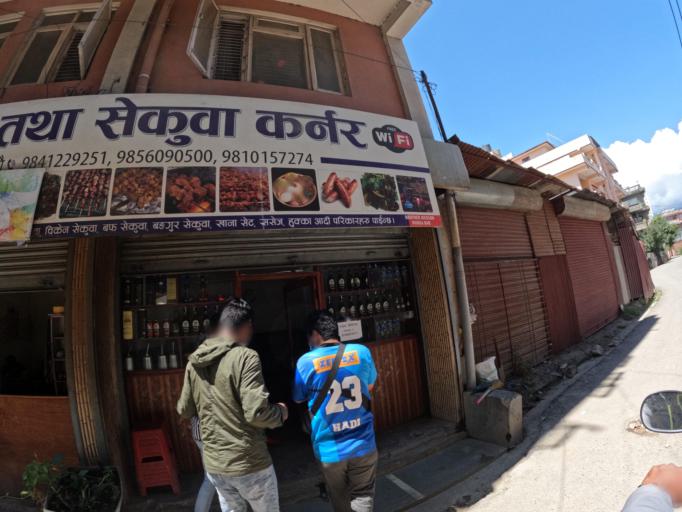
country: NP
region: Central Region
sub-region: Bagmati Zone
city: Kathmandu
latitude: 27.7371
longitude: 85.3223
